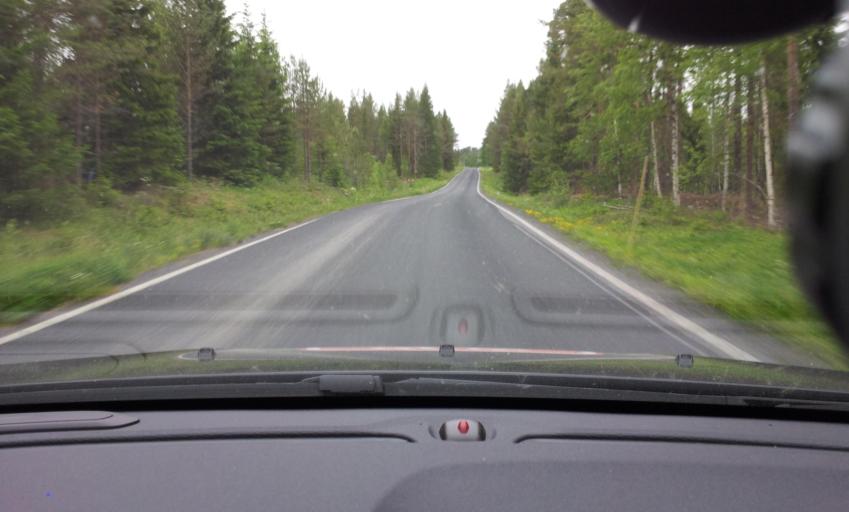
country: SE
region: Jaemtland
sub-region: Krokoms Kommun
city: Valla
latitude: 63.2972
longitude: 13.8419
